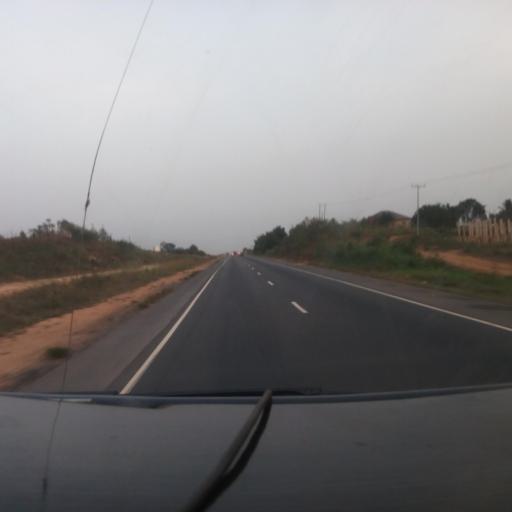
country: GH
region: Eastern
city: Nsawam
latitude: 5.8834
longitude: -0.3764
